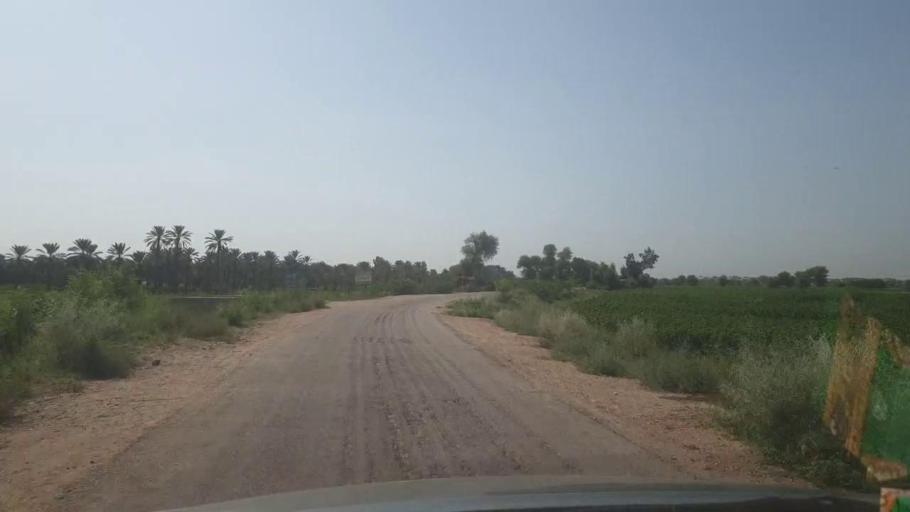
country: PK
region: Sindh
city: Rohri
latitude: 27.4698
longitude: 69.0359
